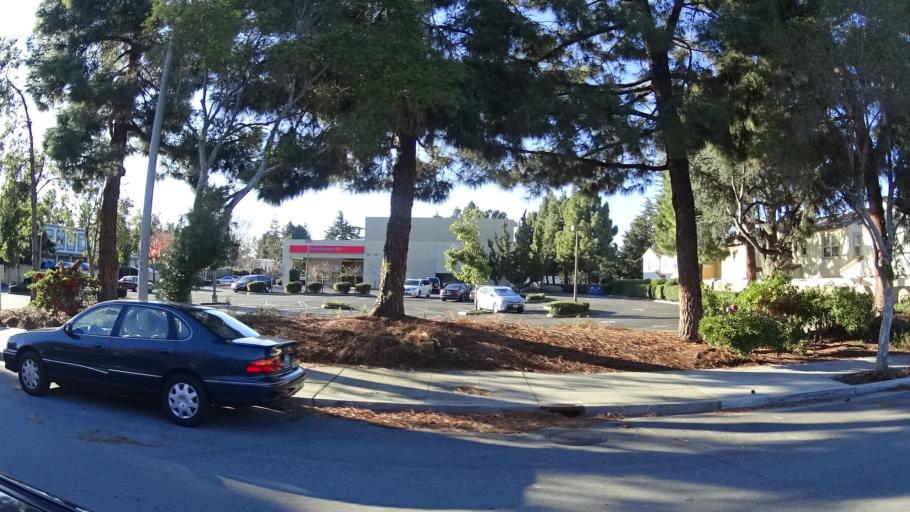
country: US
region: California
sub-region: Santa Clara County
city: Sunnyvale
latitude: 37.3721
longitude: -122.0340
